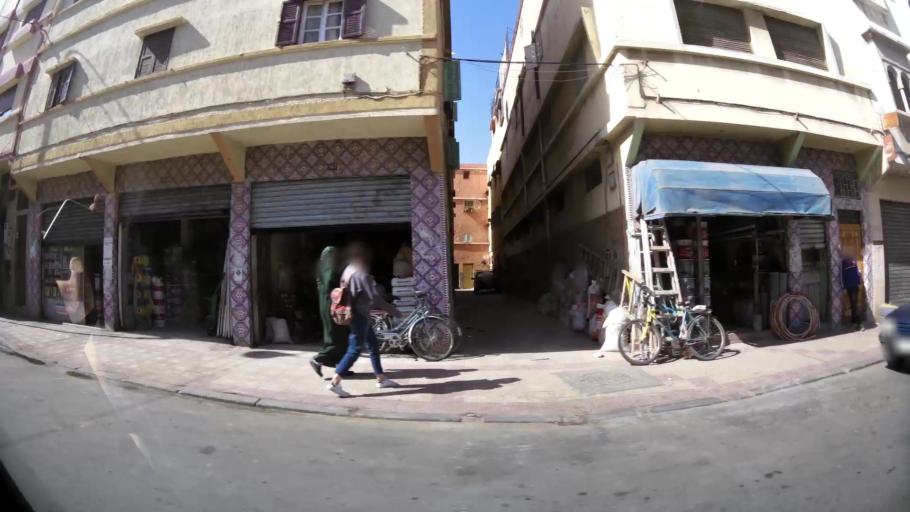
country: MA
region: Souss-Massa-Draa
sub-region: Inezgane-Ait Mellou
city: Inezgane
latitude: 30.3718
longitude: -9.5440
